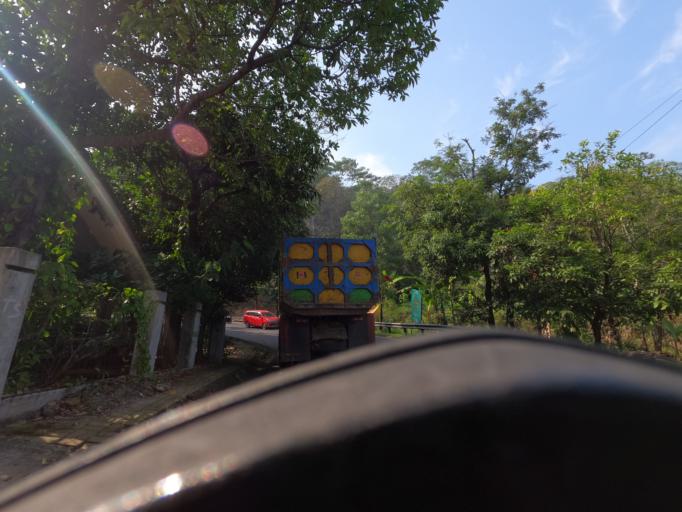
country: ID
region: West Java
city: Lembang
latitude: -6.6321
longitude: 107.7212
